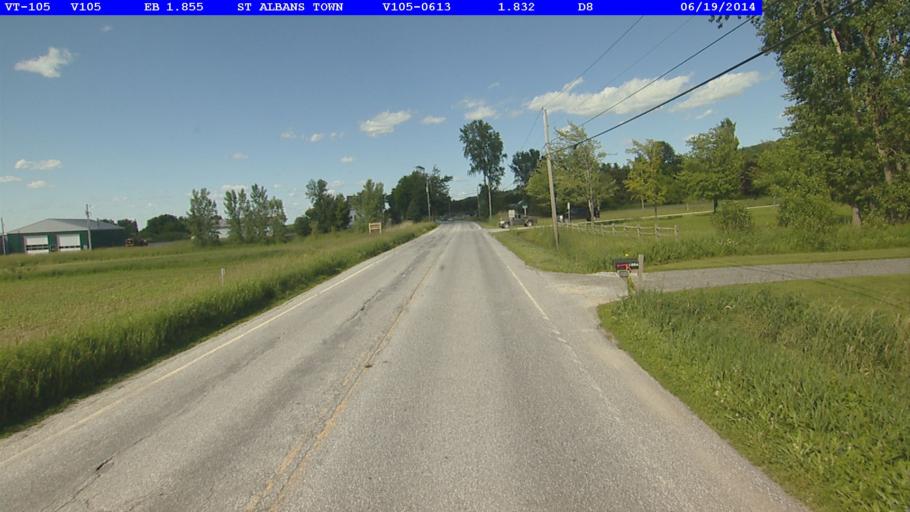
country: US
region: Vermont
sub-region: Franklin County
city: Saint Albans
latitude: 44.8335
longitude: -73.0490
